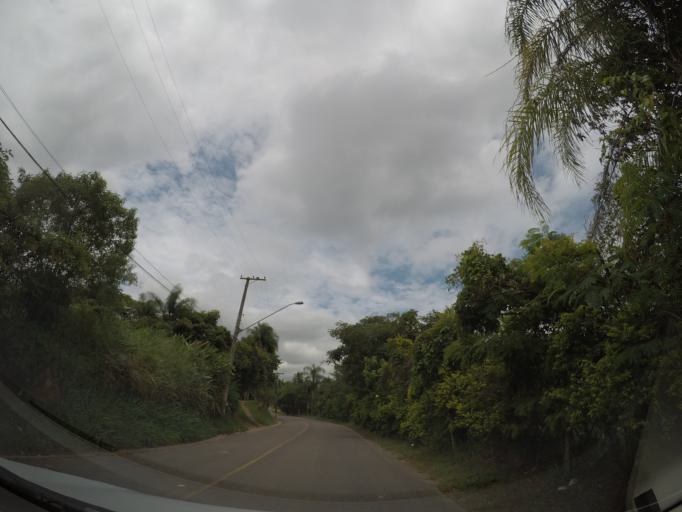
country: BR
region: Sao Paulo
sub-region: Louveira
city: Louveira
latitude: -23.0972
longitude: -46.9897
